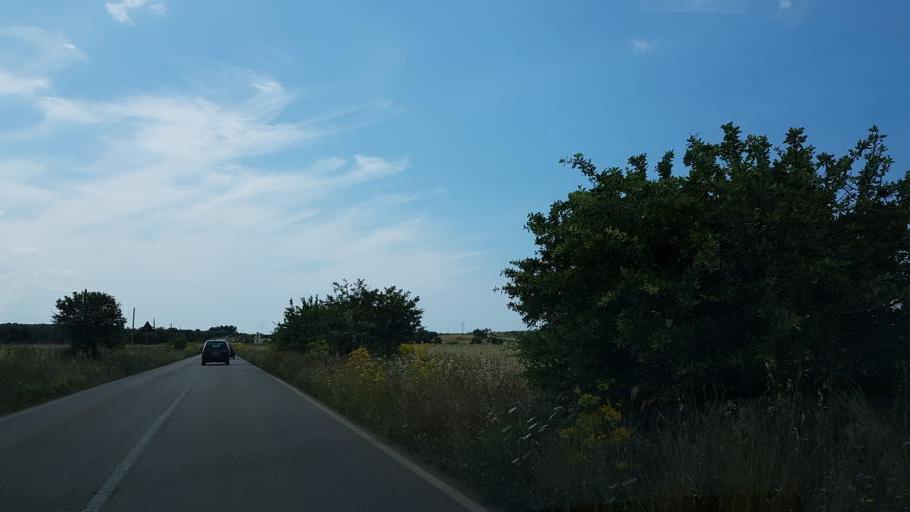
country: IT
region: Apulia
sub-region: Provincia di Brindisi
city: San Pancrazio Salentino
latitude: 40.3345
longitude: 17.8509
